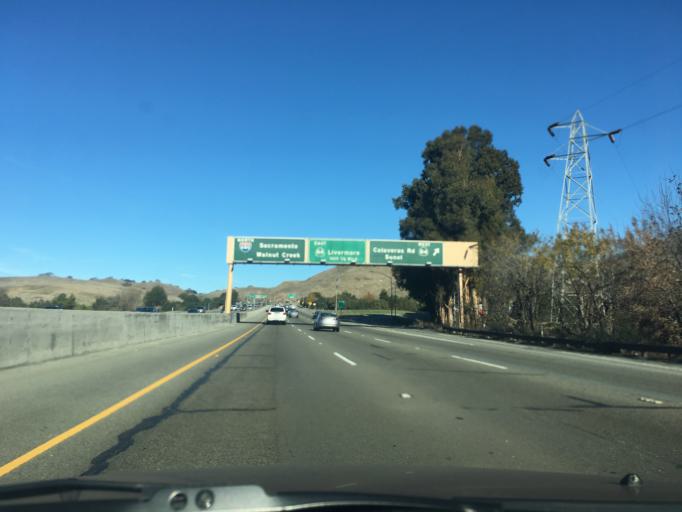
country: US
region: California
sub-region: Alameda County
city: Pleasanton
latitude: 37.5851
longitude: -121.8728
